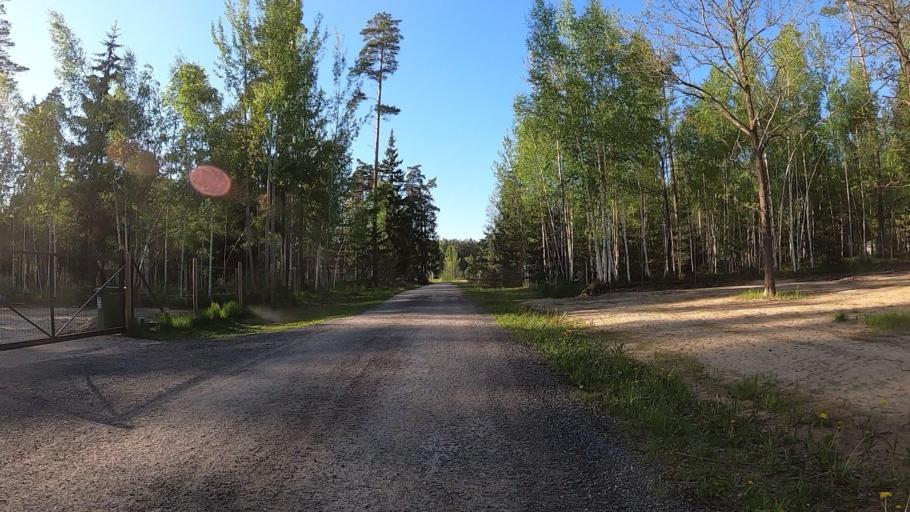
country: LV
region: Baldone
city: Baldone
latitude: 56.7759
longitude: 24.3091
